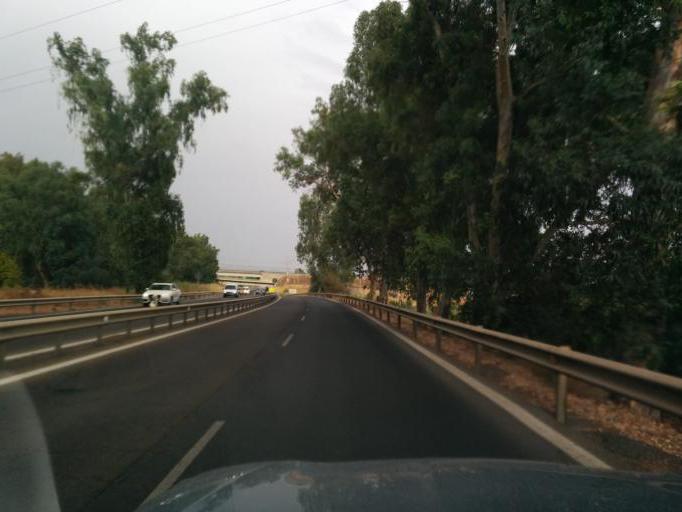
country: ES
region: Andalusia
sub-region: Provincia de Sevilla
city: Sevilla
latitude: 37.4240
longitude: -5.9540
